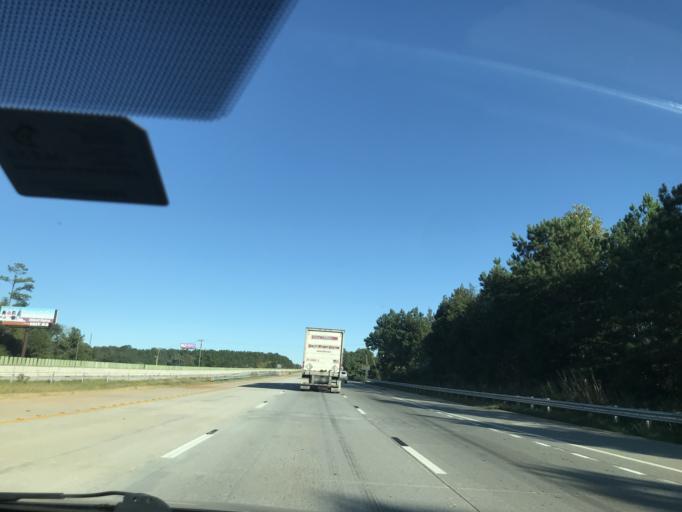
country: US
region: South Carolina
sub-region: Spartanburg County
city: Valley Falls
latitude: 35.0126
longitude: -81.9514
